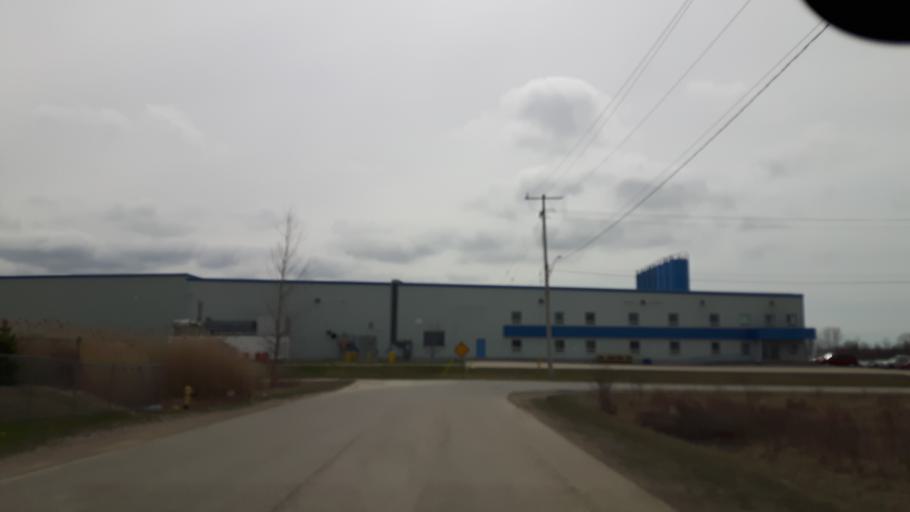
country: CA
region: Ontario
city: Goderich
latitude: 43.7230
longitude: -81.7030
